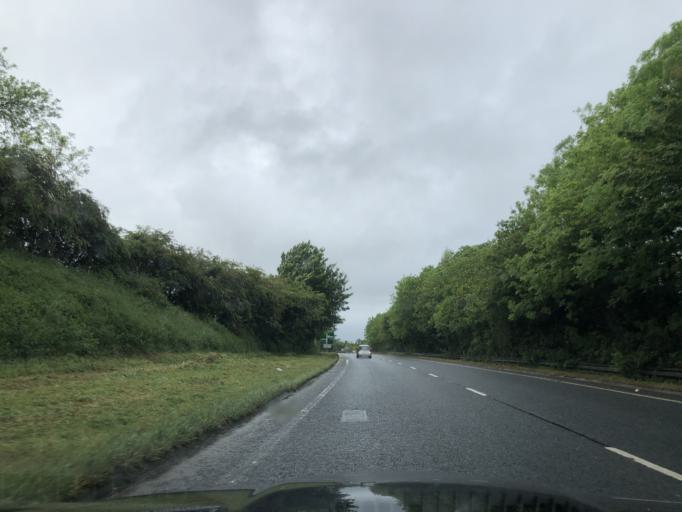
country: GB
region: Northern Ireland
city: Connor
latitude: 54.7762
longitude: -6.2453
